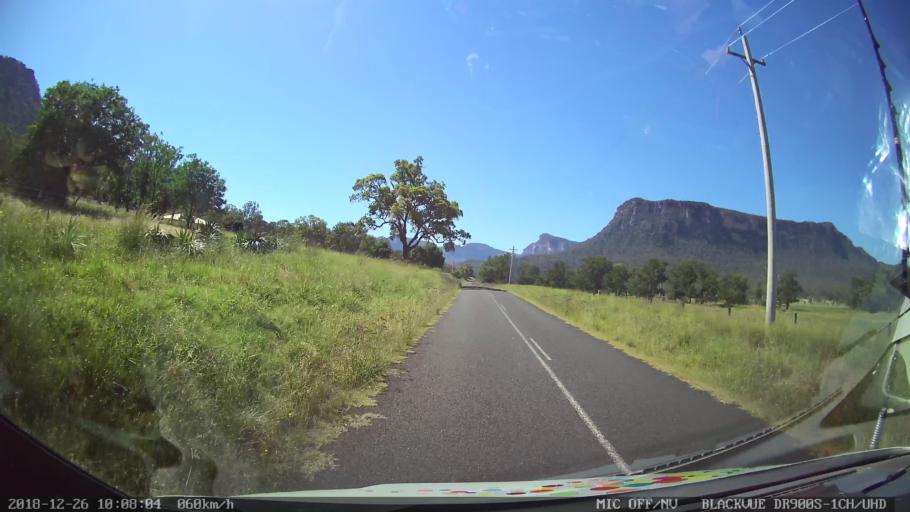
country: AU
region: New South Wales
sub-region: Mid-Western Regional
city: Kandos
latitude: -33.0947
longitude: 150.2282
